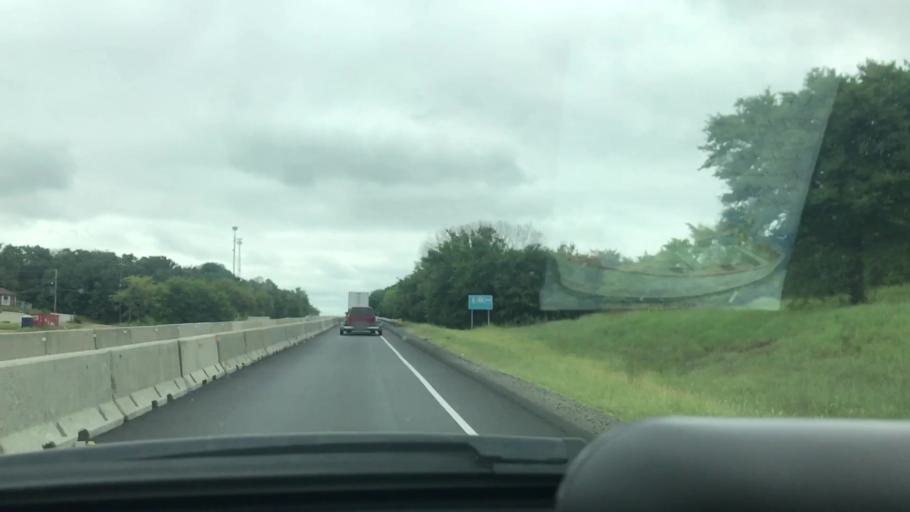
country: US
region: Oklahoma
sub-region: McIntosh County
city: Eufaula
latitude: 35.2829
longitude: -95.5931
